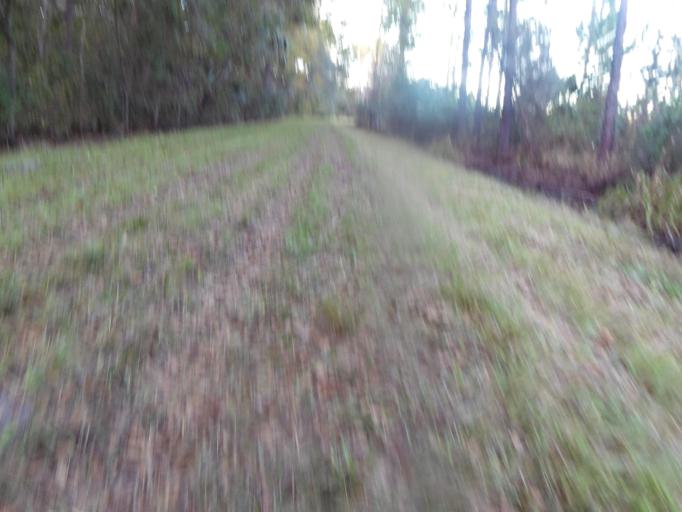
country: US
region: Florida
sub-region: Putnam County
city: Palatka
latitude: 29.6726
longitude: -81.7553
